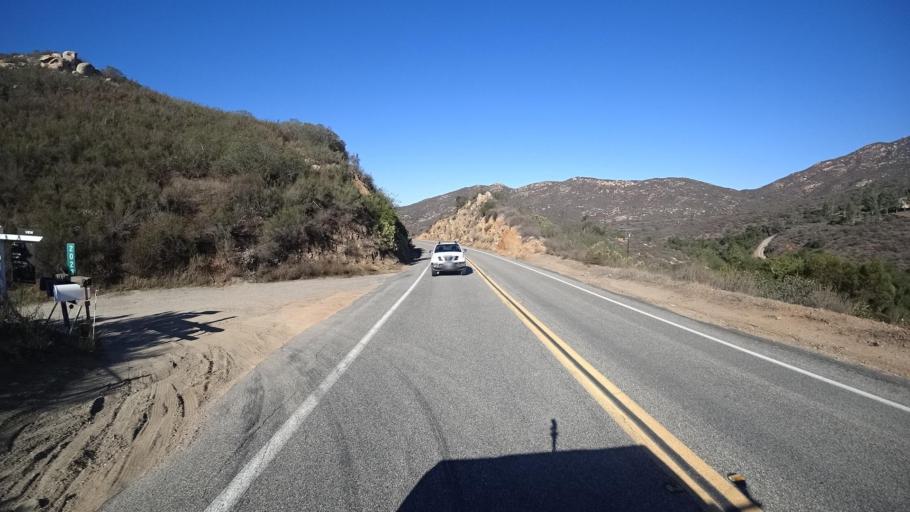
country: US
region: California
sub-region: San Diego County
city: Jamul
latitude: 32.6726
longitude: -116.7771
